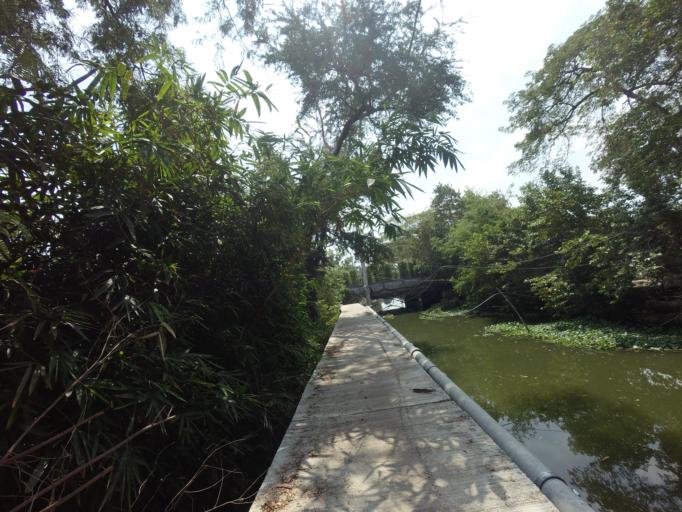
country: TH
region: Bangkok
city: Saphan Sung
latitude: 13.7579
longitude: 100.6696
